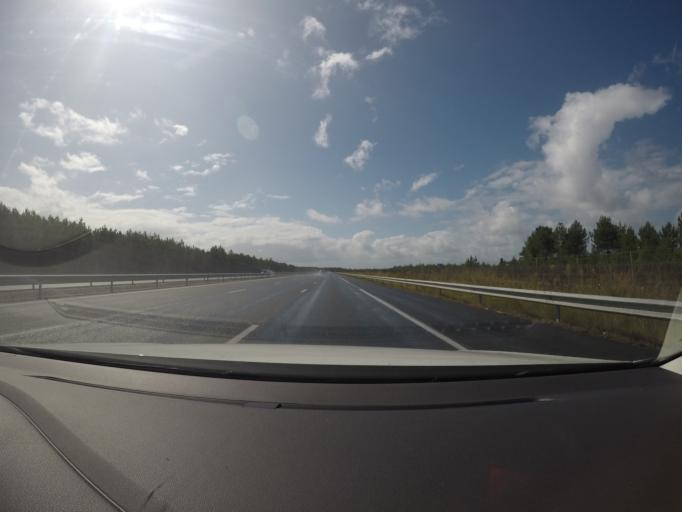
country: FR
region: Aquitaine
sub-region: Departement des Landes
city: Castets
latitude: 43.9073
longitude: -1.1249
